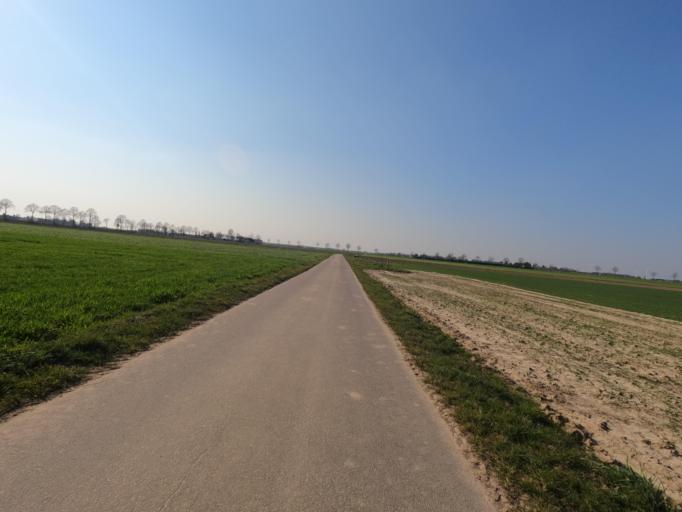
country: DE
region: North Rhine-Westphalia
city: Erkelenz
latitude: 51.0932
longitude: 6.2697
